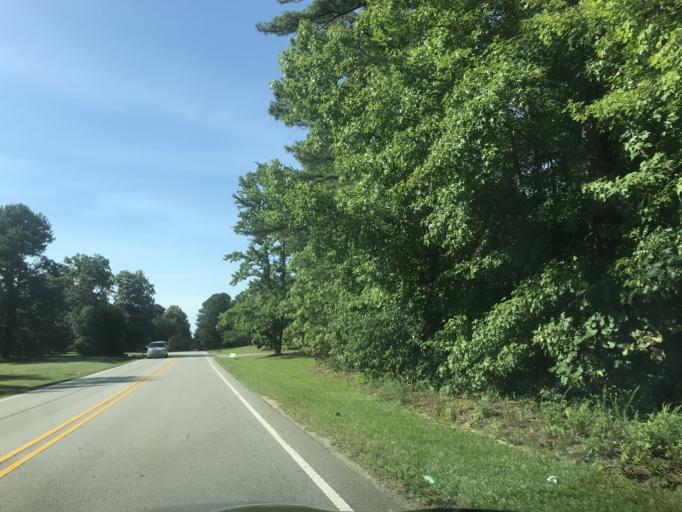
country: US
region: North Carolina
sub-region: Wake County
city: Garner
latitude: 35.6762
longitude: -78.5772
